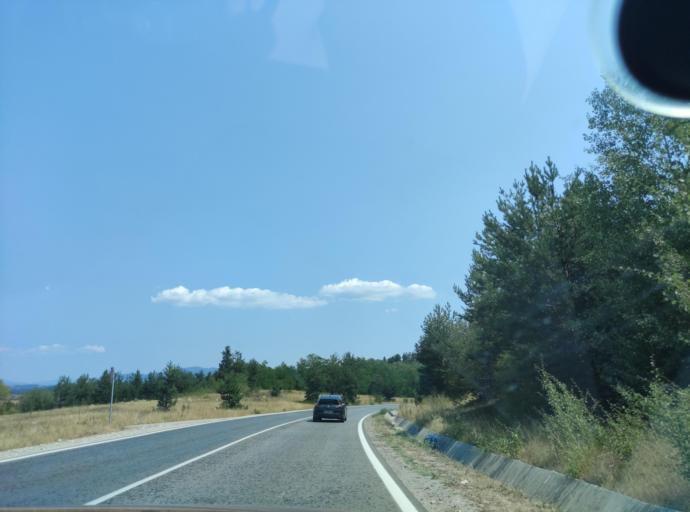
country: BG
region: Blagoevgrad
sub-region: Obshtina Razlog
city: Razlog
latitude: 41.8871
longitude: 23.5028
